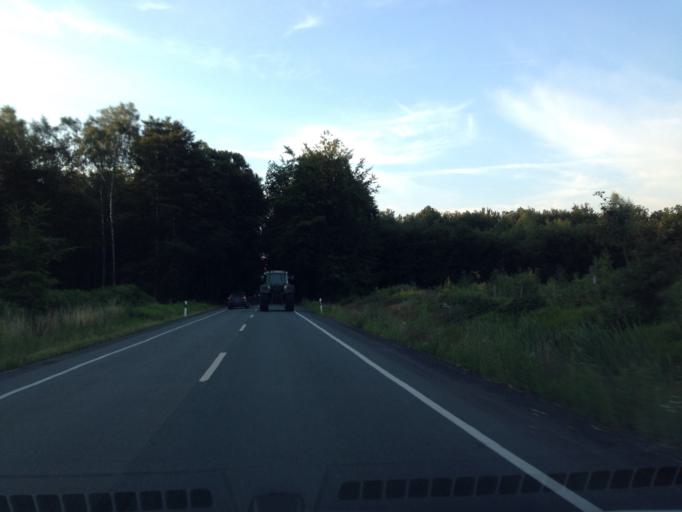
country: DE
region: North Rhine-Westphalia
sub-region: Regierungsbezirk Munster
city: Senden
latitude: 51.8382
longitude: 7.5427
